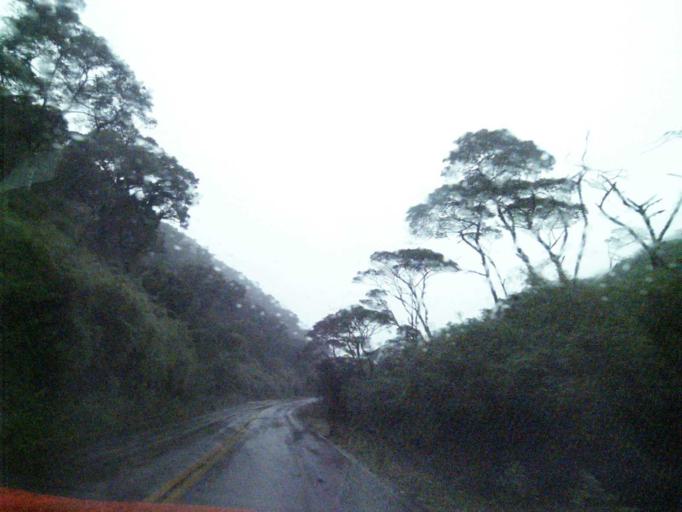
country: BR
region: Santa Catarina
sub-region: Anitapolis
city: Anitapolis
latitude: -27.7639
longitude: -49.0391
